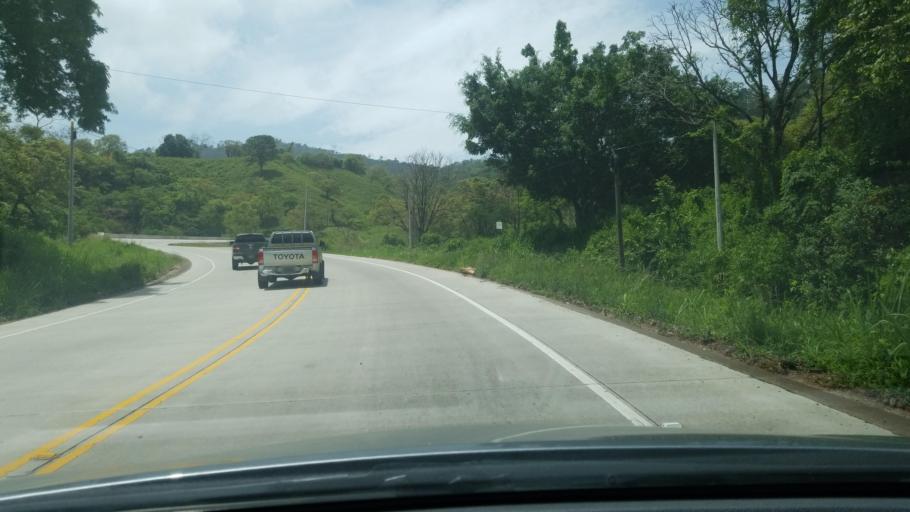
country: HN
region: Copan
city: Agua Caliente
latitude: 14.8764
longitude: -88.7790
